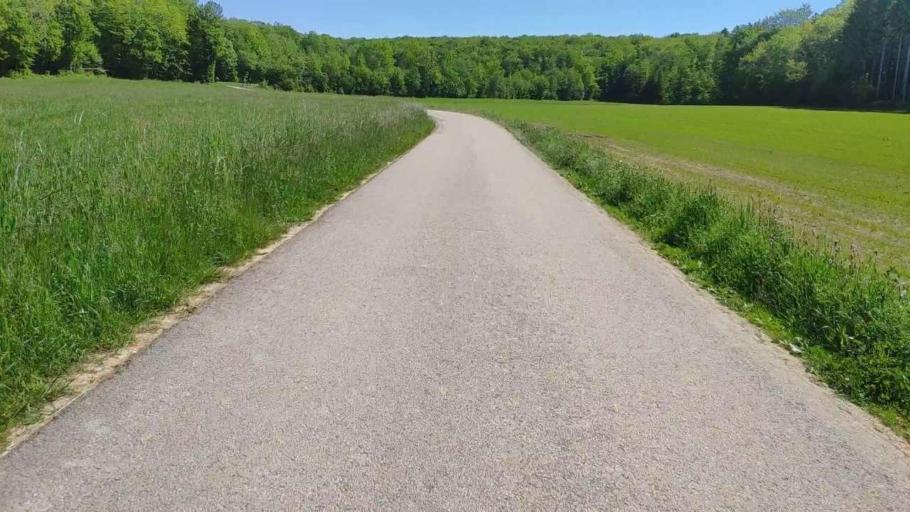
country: FR
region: Franche-Comte
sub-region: Departement du Jura
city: Poligny
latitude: 46.7409
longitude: 5.7714
